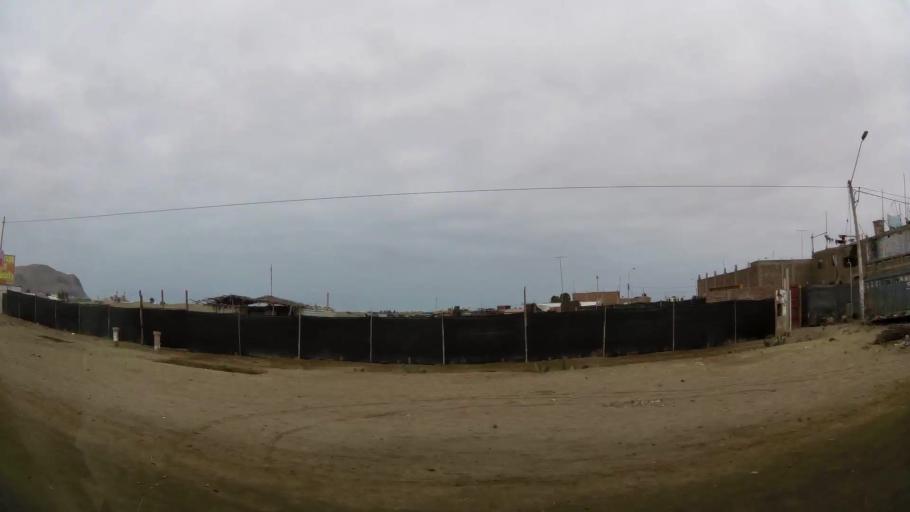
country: PE
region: Lima
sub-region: Provincia de Canete
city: Chilca
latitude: -12.5229
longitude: -76.7300
